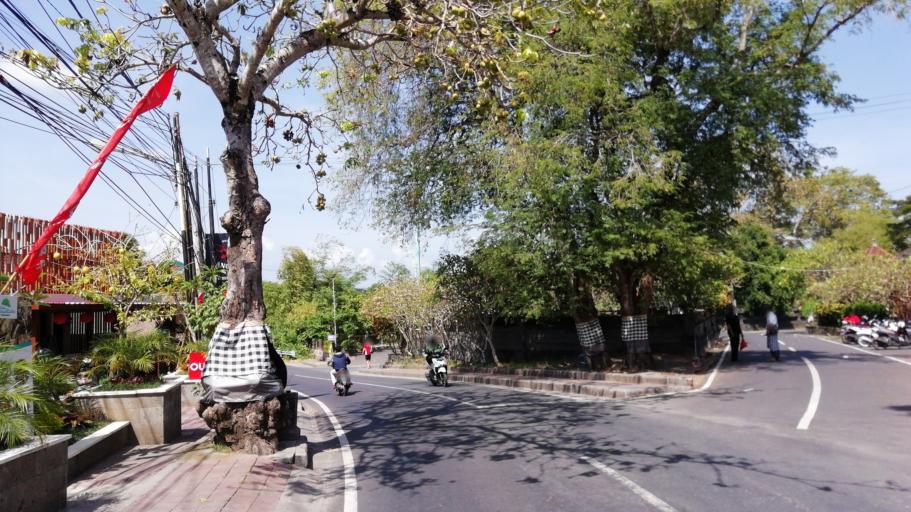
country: ID
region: Bali
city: Banjar Gunungpande
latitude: -8.6420
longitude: 115.1423
